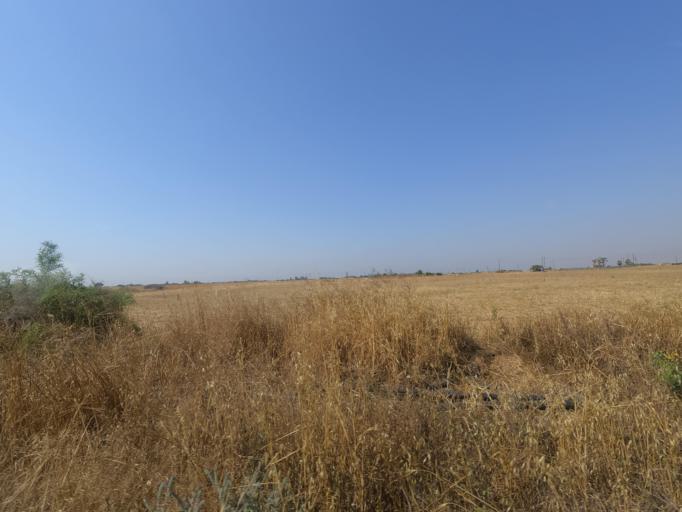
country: CY
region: Ammochostos
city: Avgorou
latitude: 35.0594
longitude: 33.8655
